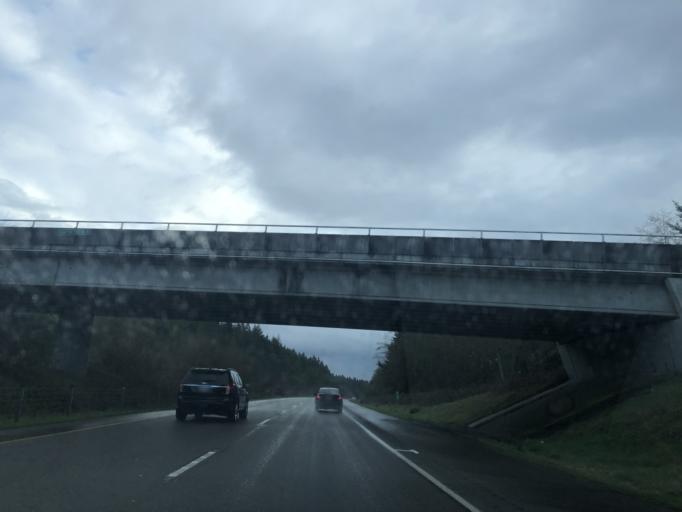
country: US
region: Washington
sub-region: Pierce County
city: Purdy
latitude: 47.3895
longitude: -122.6167
